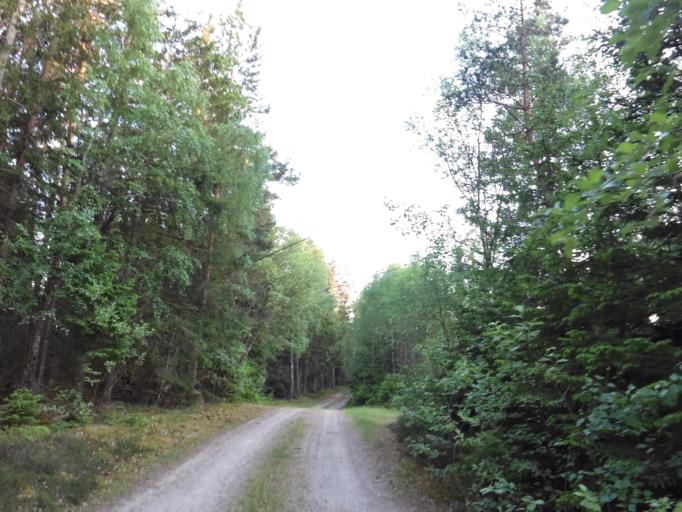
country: SE
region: Blekinge
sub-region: Olofstroms Kommun
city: Olofstroem
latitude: 56.4057
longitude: 14.5426
